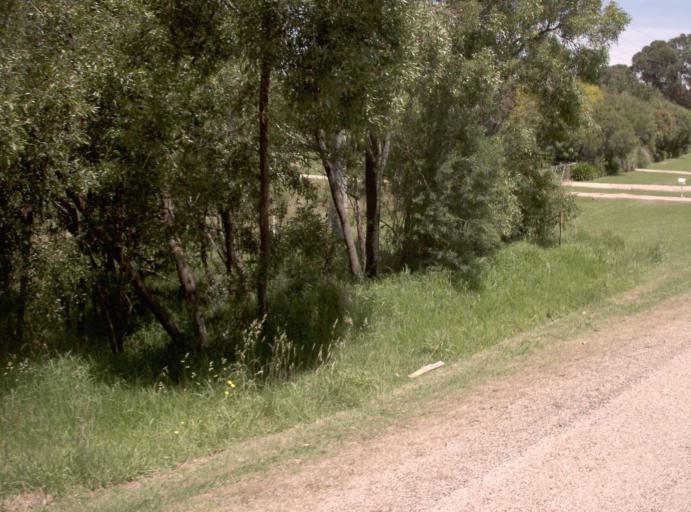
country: AU
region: Victoria
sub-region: East Gippsland
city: Bairnsdale
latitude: -37.7503
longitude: 147.7315
